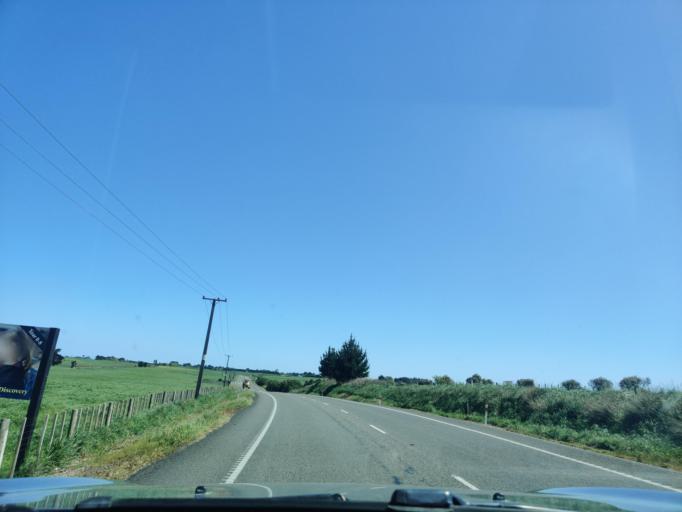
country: NZ
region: Taranaki
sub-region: South Taranaki District
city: Patea
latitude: -39.7710
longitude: 174.6689
